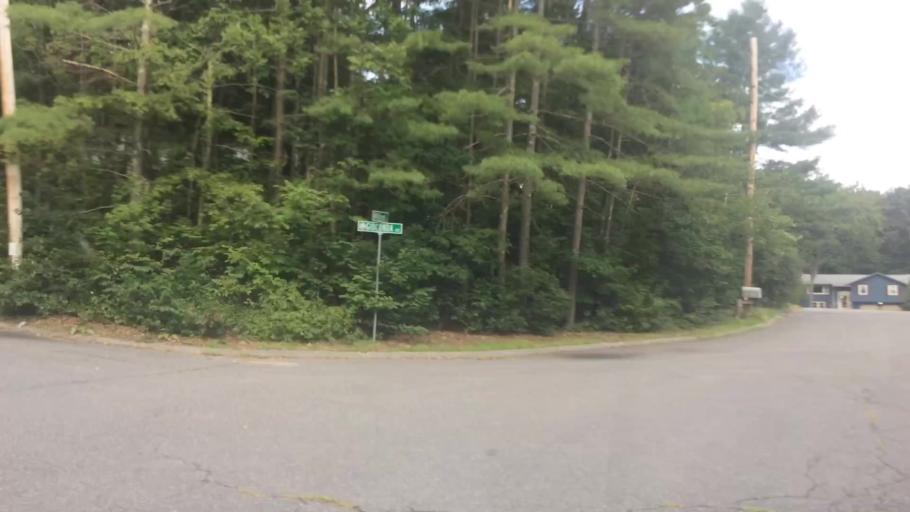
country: US
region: Massachusetts
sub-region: Middlesex County
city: Acton
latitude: 42.4611
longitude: -71.4371
